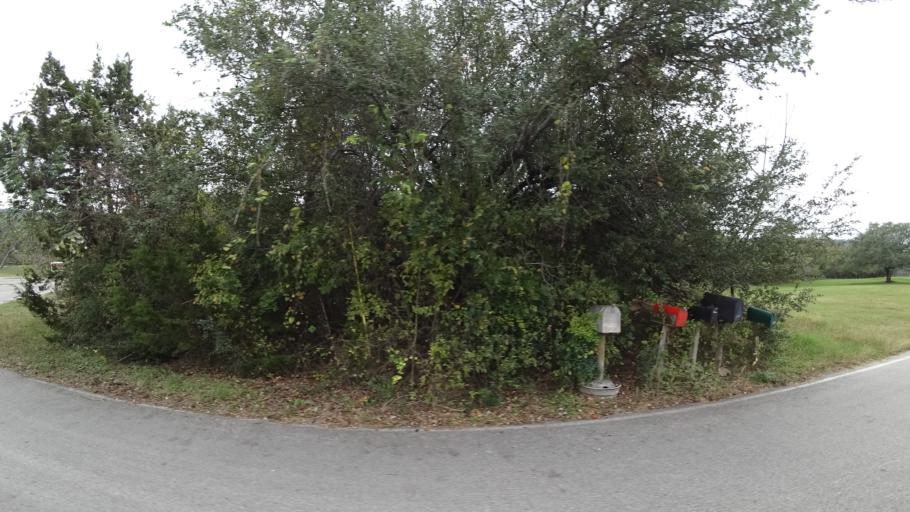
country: US
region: Texas
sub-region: Travis County
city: Bee Cave
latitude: 30.3383
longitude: -97.9051
